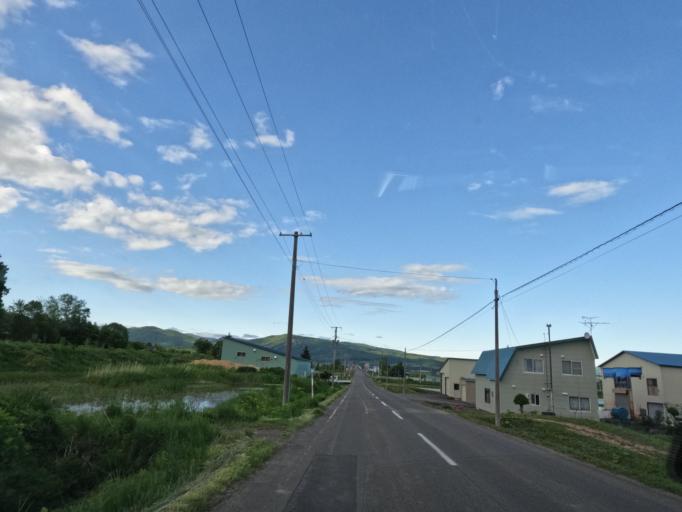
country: JP
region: Hokkaido
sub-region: Asahikawa-shi
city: Asahikawa
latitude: 43.8845
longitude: 142.4586
